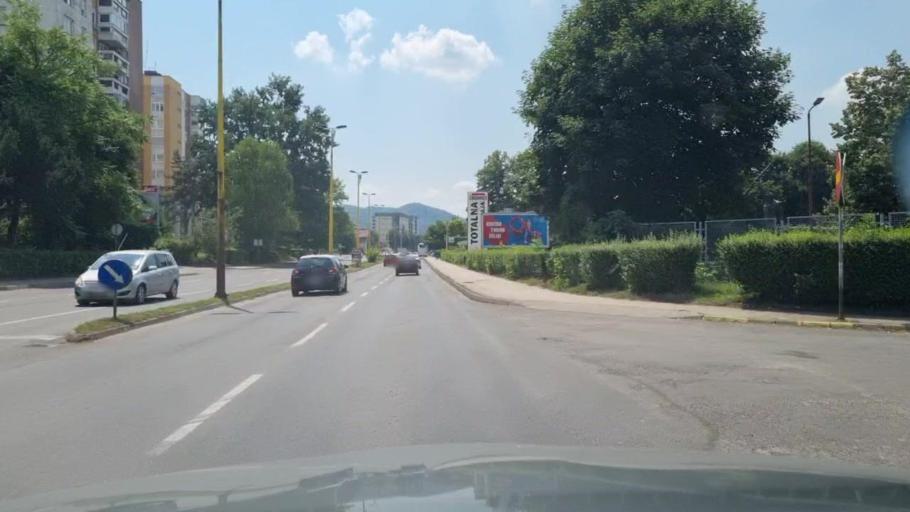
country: BA
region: Federation of Bosnia and Herzegovina
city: Tuzla
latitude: 44.5341
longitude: 18.6573
